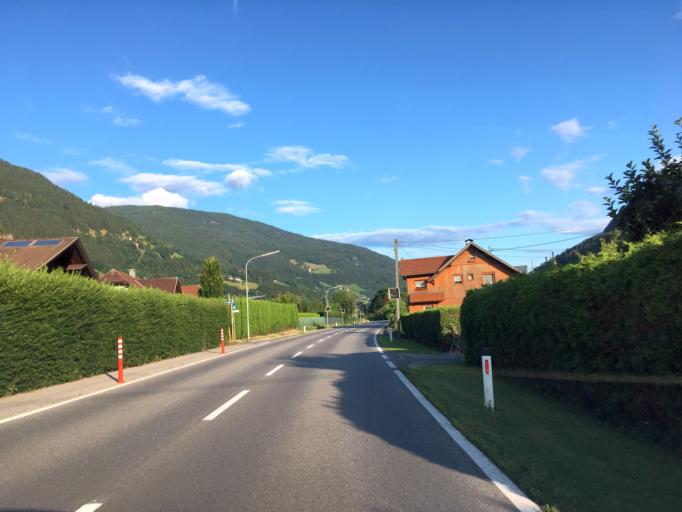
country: AT
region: Carinthia
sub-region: Politischer Bezirk Spittal an der Drau
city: Radenthein
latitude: 46.7902
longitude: 13.7284
